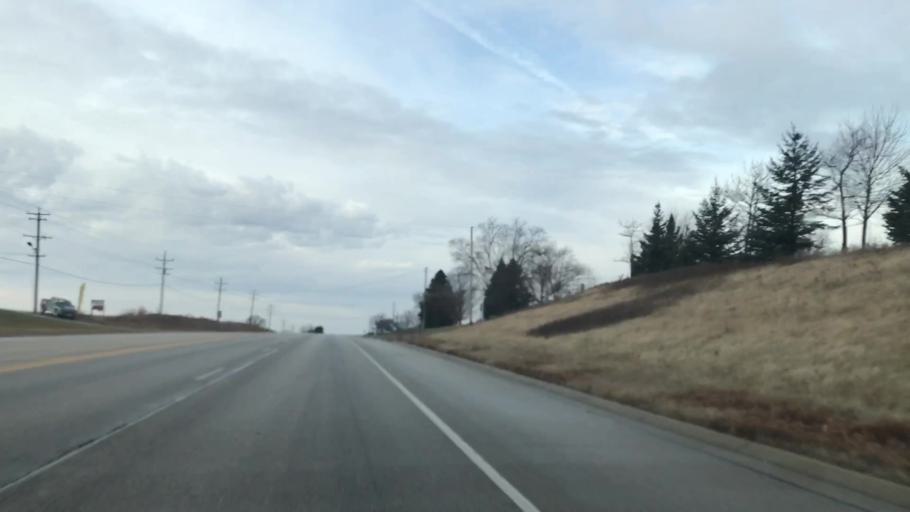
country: US
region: Wisconsin
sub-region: Washington County
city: West Bend
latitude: 43.4276
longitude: -88.2652
